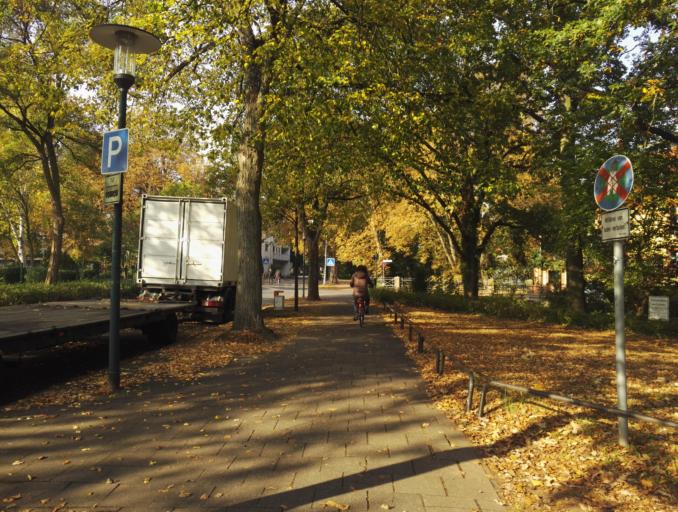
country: DE
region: Lower Saxony
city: Hameln
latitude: 52.1055
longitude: 9.3641
